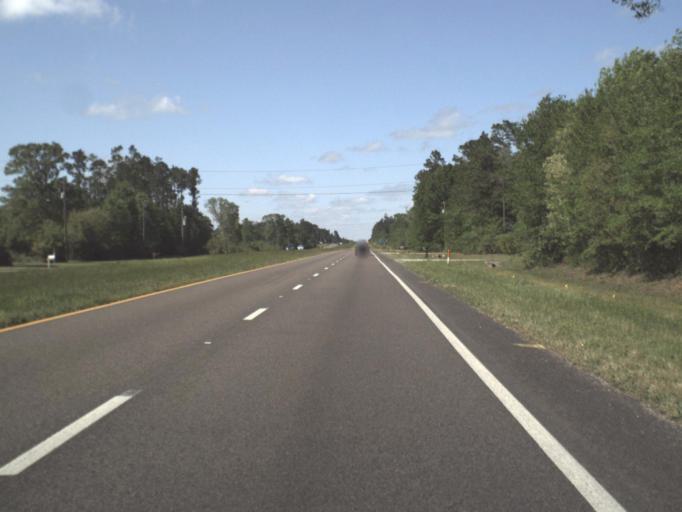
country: US
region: Florida
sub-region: Escambia County
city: Cantonment
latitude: 30.6668
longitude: -87.3513
